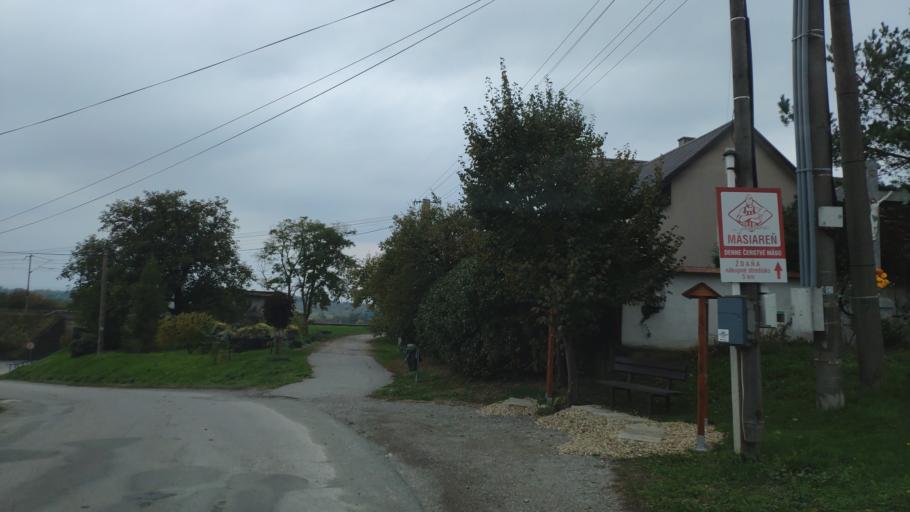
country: SK
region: Kosicky
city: Kosice
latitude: 48.6366
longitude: 21.3832
